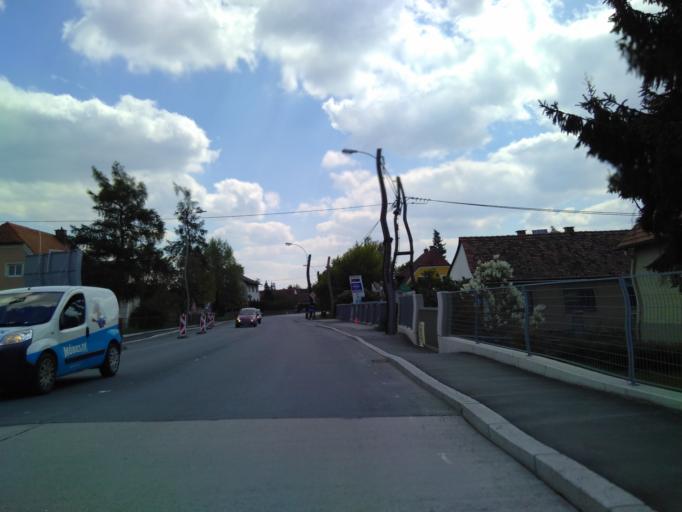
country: AT
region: Styria
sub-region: Politischer Bezirk Graz-Umgebung
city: Feldkirchen bei Graz
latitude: 47.0299
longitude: 15.4656
